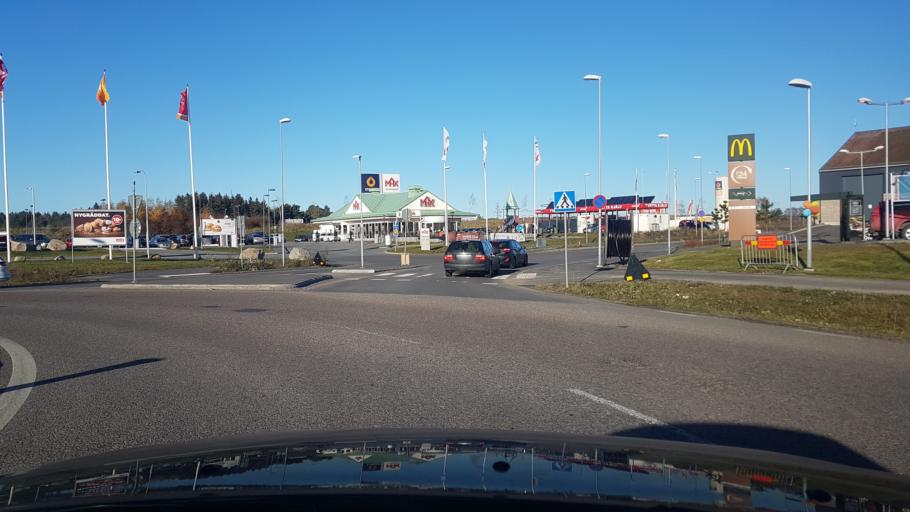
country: SE
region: Uppsala
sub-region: Uppsala Kommun
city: Gamla Uppsala
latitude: 59.8850
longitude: 17.6679
